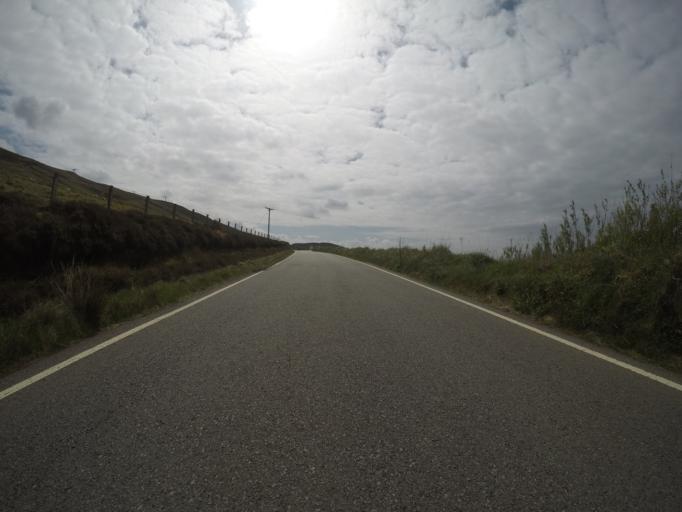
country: GB
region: Scotland
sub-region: Highland
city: Portree
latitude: 57.6108
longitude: -6.3732
